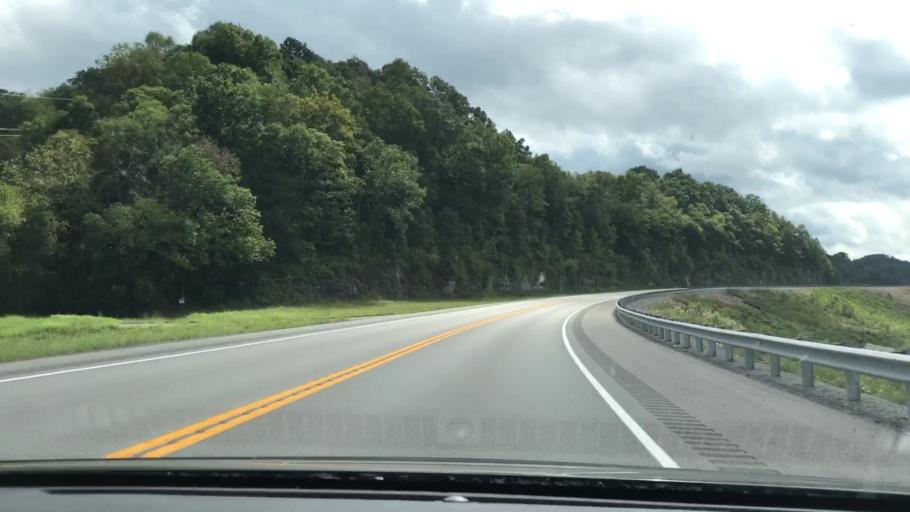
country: US
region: Kentucky
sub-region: Cumberland County
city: Burkesville
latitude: 36.7983
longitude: -85.4154
